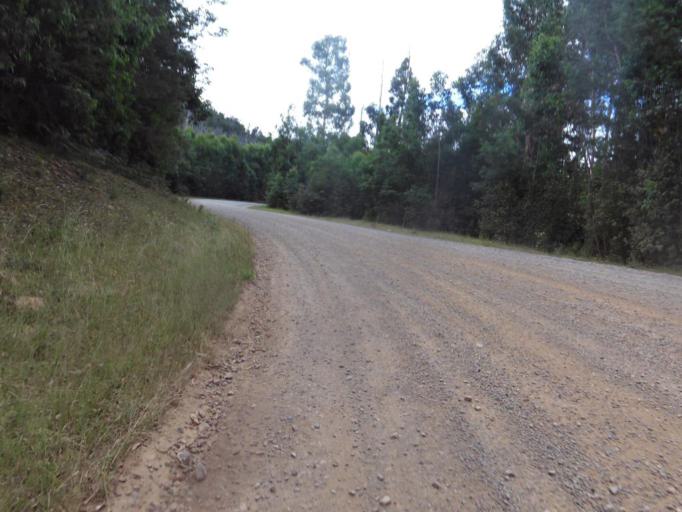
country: AU
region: Victoria
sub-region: Yarra Ranges
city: Healesville
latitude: -37.4013
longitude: 145.5607
